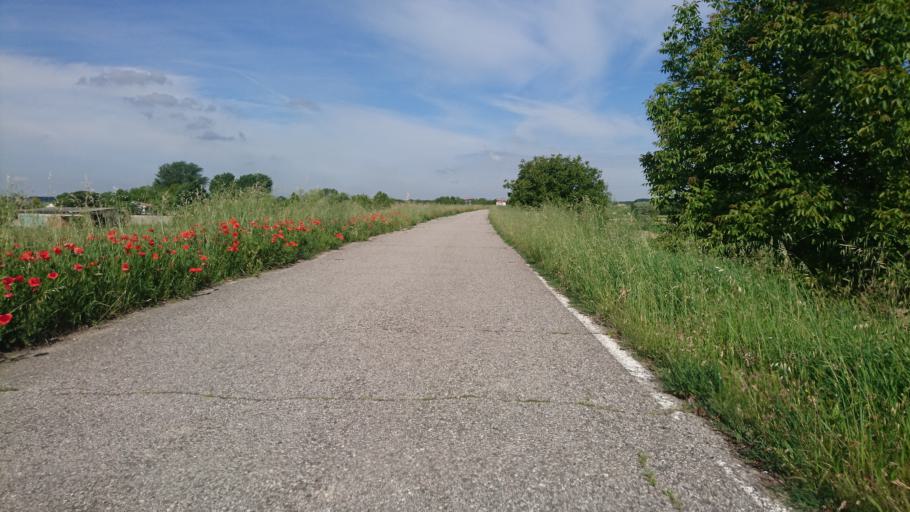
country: IT
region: Lombardy
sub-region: Provincia di Mantova
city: Carbonara di Po
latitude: 45.0404
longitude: 11.2219
